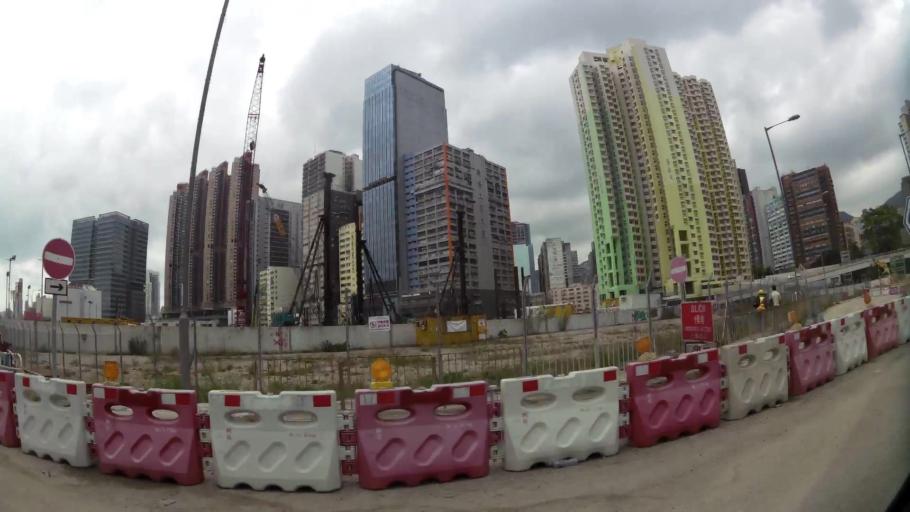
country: HK
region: Wong Tai Sin
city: Wong Tai Sin
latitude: 22.3338
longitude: 114.2014
